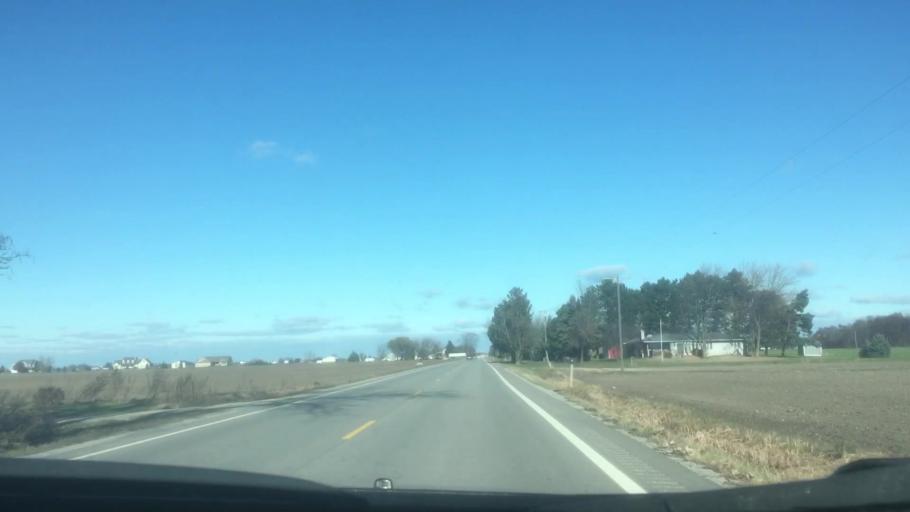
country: US
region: Michigan
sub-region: Bay County
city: Essexville
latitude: 43.5459
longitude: -83.7589
